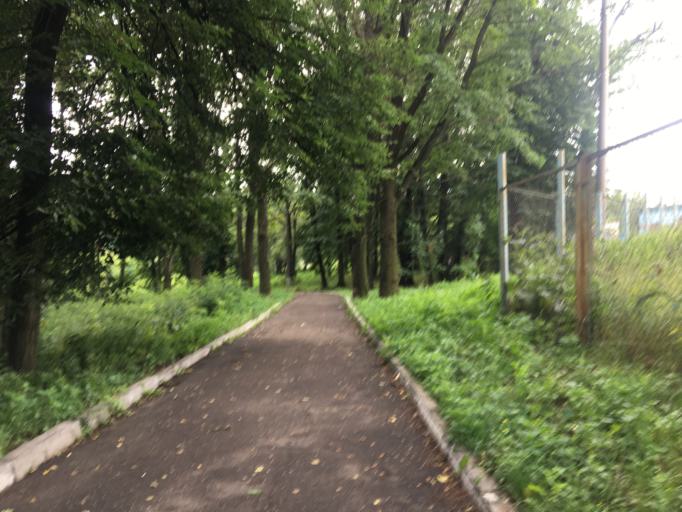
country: RU
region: Tula
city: Tula
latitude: 54.1739
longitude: 37.6047
